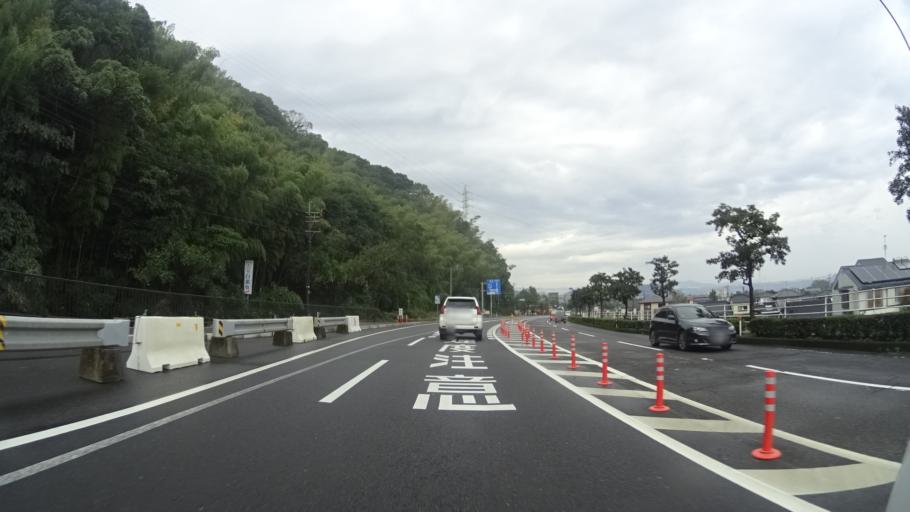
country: JP
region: Kagoshima
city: Kajiki
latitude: 31.7008
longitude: 130.6117
